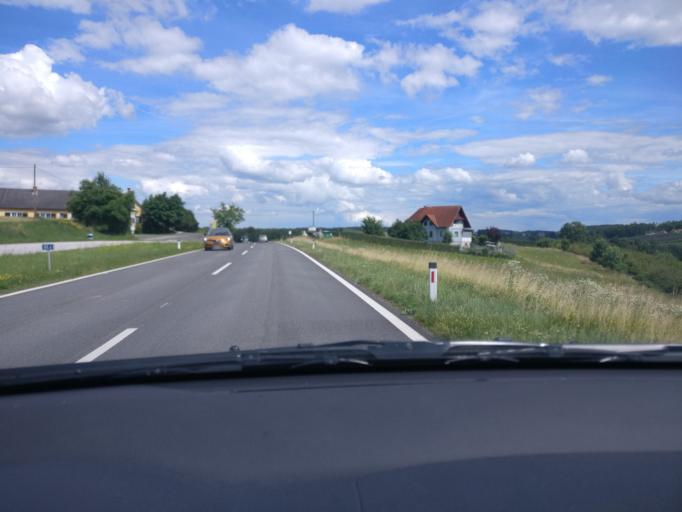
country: AT
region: Styria
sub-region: Politischer Bezirk Hartberg-Fuerstenfeld
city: Dienersdorf
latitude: 47.2135
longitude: 15.8616
